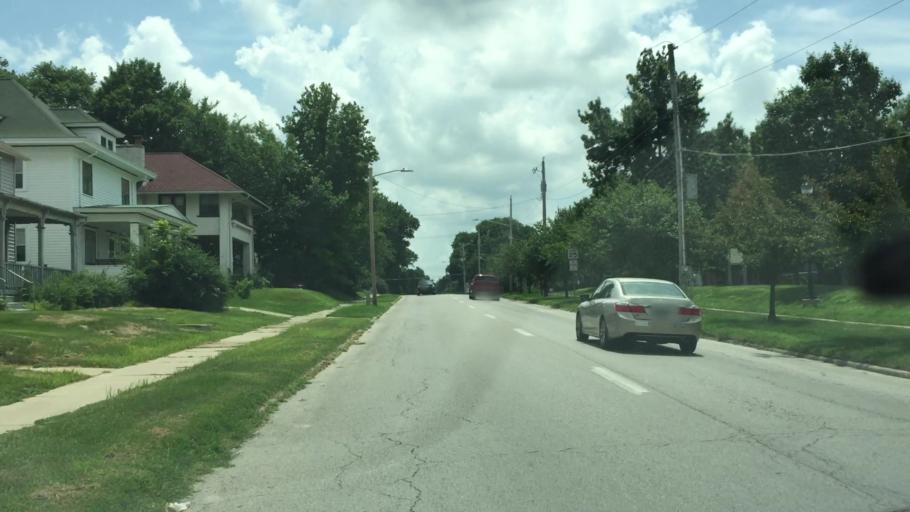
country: US
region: Iowa
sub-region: Johnson County
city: Iowa City
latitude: 41.6599
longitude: -91.5258
